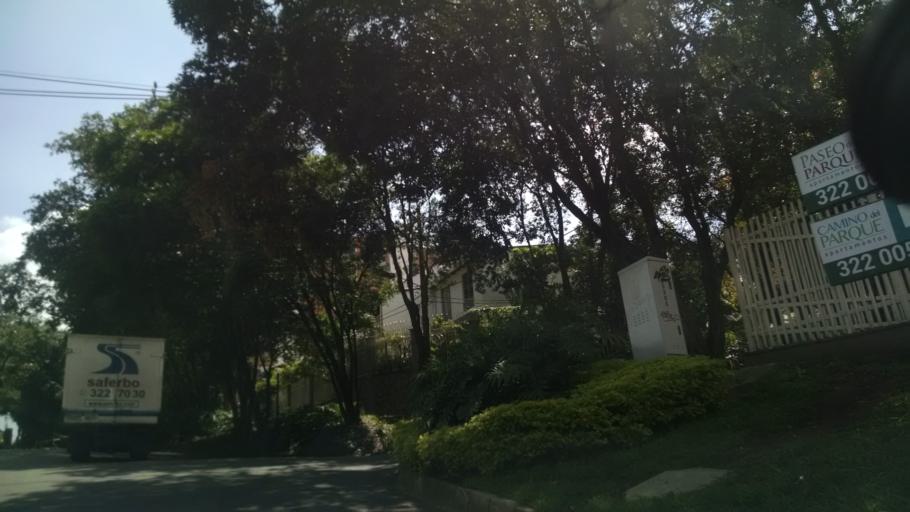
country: CO
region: Antioquia
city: Itagui
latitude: 6.2206
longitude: -75.6040
